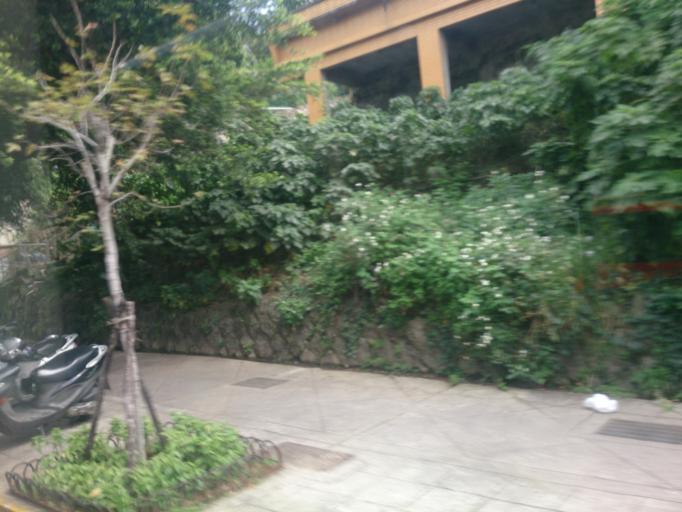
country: TW
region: Taipei
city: Taipei
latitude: 25.0866
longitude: 121.5262
